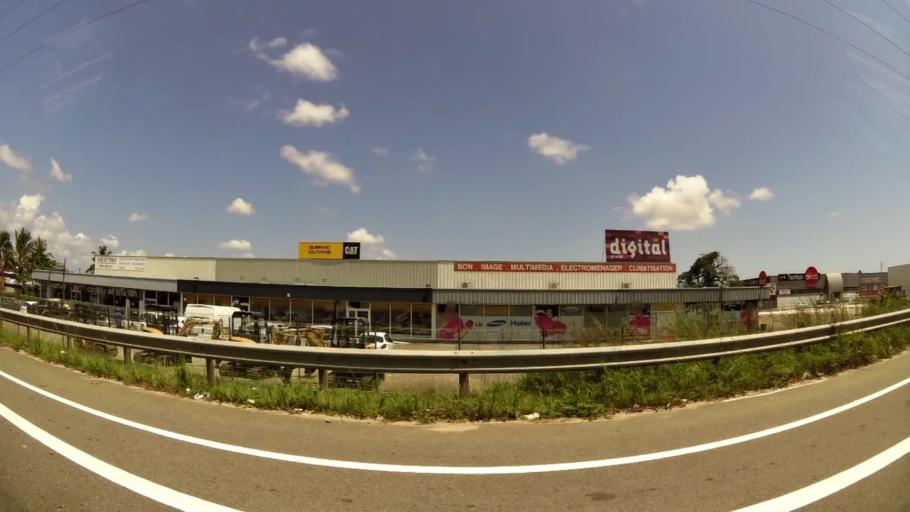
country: GF
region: Guyane
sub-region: Guyane
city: Cayenne
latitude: 4.9042
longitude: -52.3239
